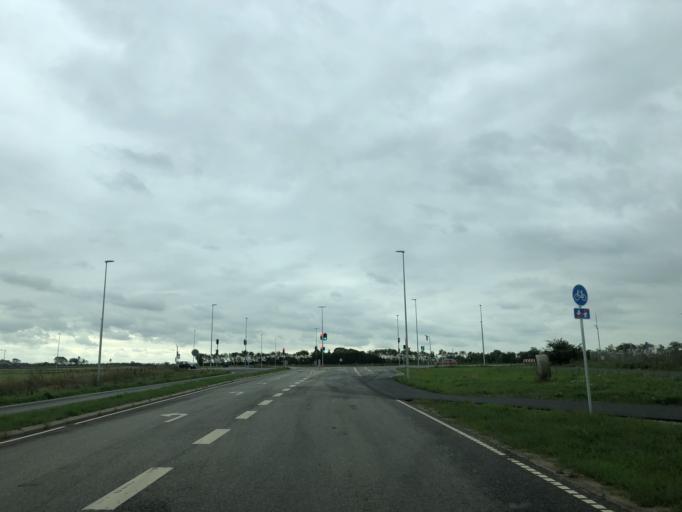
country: DK
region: Central Jutland
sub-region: Herning Kommune
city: Snejbjerg
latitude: 56.1538
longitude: 8.8935
